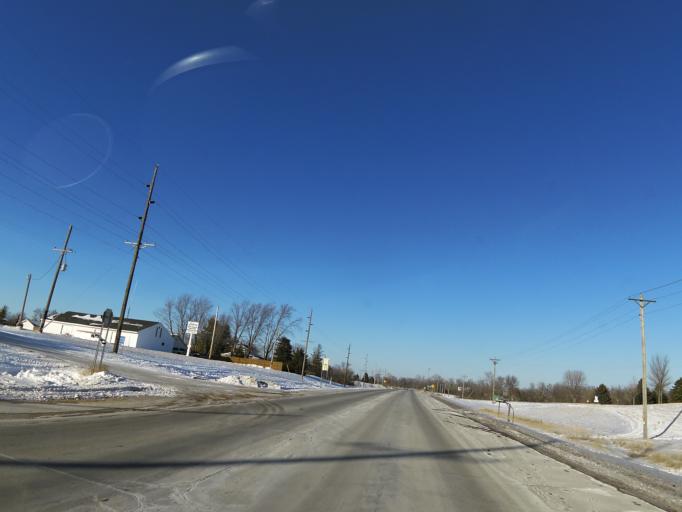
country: US
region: Minnesota
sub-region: Le Sueur County
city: New Prague
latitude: 44.5541
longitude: -93.5845
